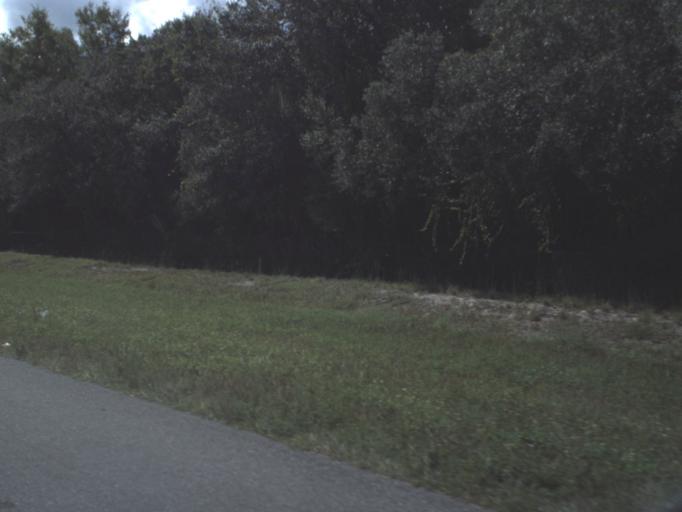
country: US
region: Florida
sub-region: Pasco County
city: Shady Hills
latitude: 28.3148
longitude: -82.5509
